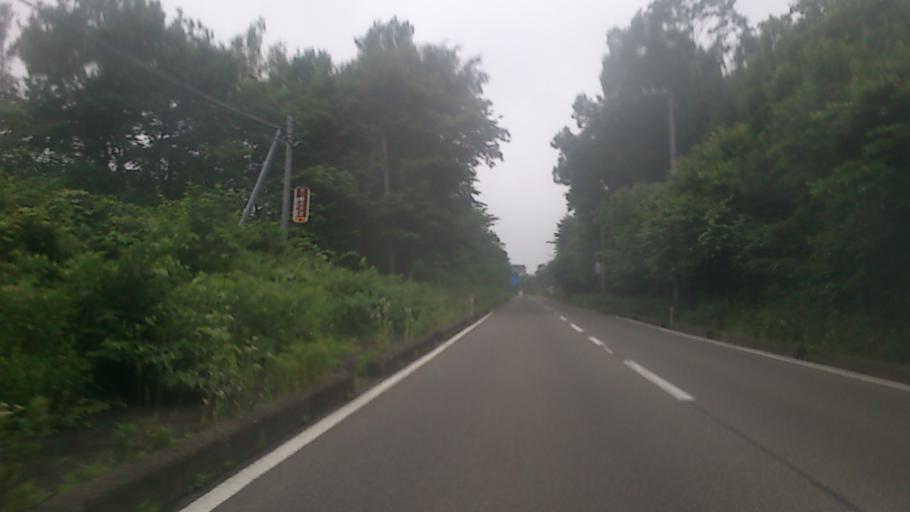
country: JP
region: Miyagi
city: Shiroishi
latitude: 38.1155
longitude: 140.5680
